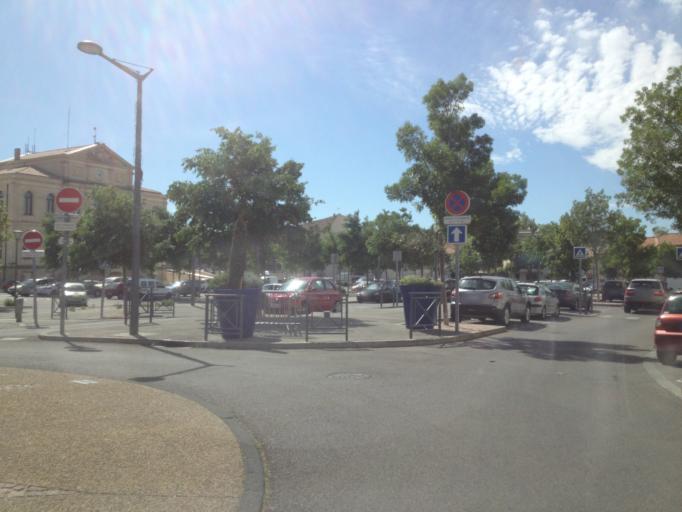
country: FR
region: Provence-Alpes-Cote d'Azur
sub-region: Departement du Vaucluse
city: Sorgues
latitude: 44.0079
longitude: 4.8743
